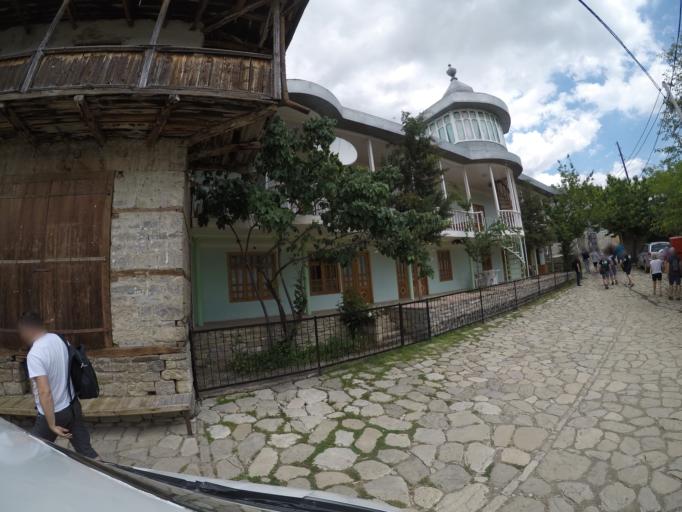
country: AZ
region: Ismayilli
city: Basqal
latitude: 40.8510
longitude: 48.3908
